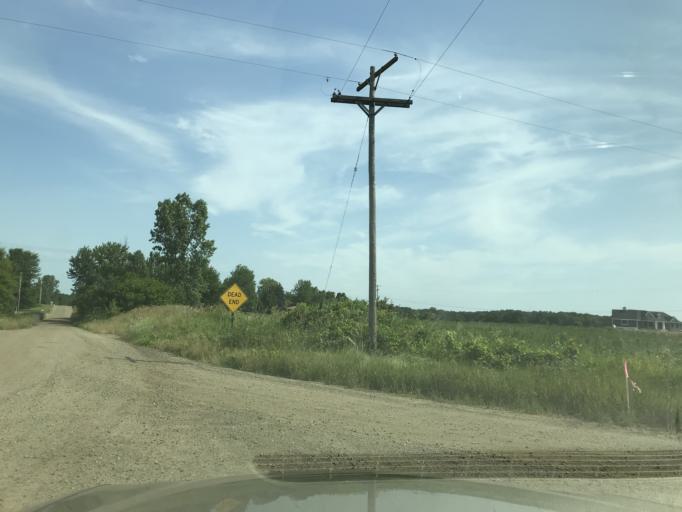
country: US
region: Michigan
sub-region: Eaton County
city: Grand Ledge
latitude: 42.7703
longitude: -84.7198
